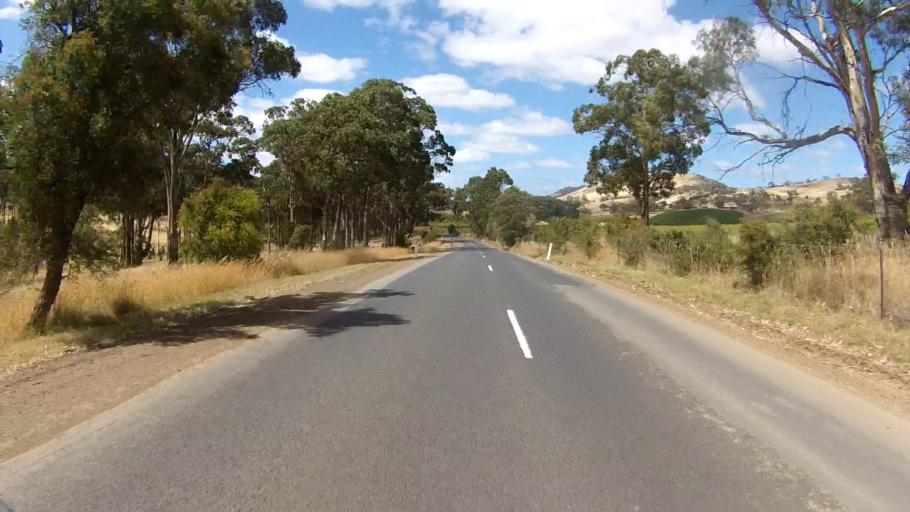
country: AU
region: Tasmania
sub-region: Sorell
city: Sorell
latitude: -42.7439
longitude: 147.4845
